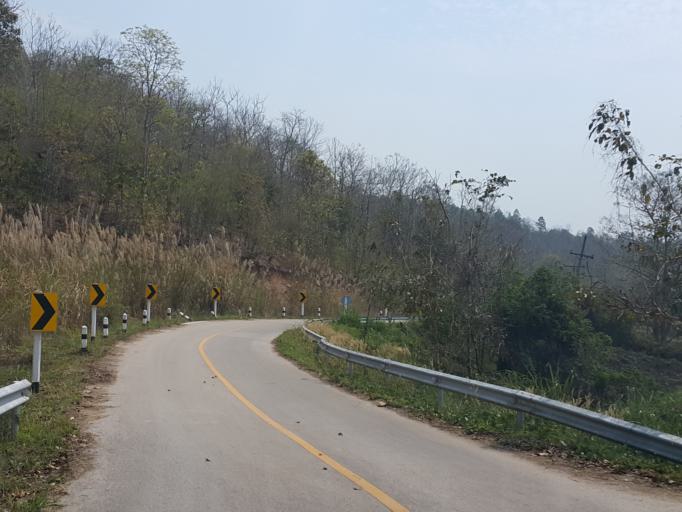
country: TH
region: Lampang
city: Mueang Pan
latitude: 18.8001
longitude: 99.4880
